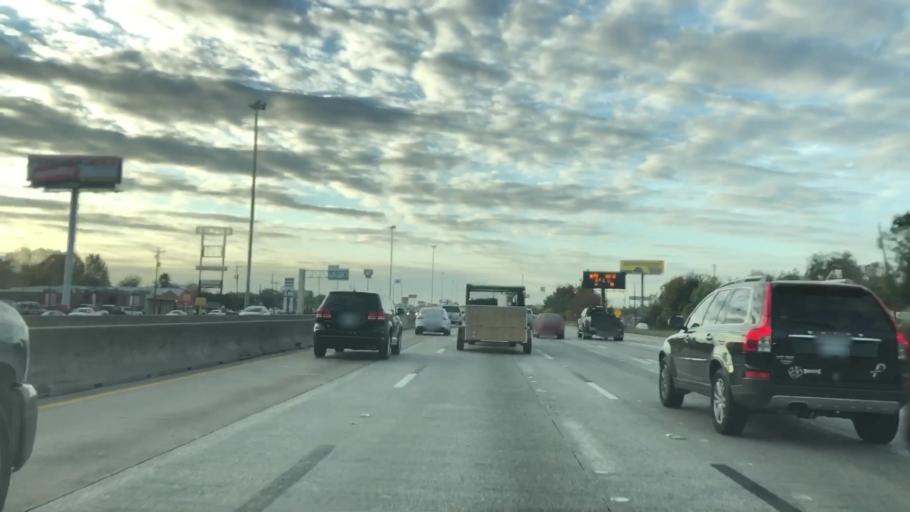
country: US
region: Texas
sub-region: Harris County
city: Aldine
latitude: 29.9031
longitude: -95.4123
